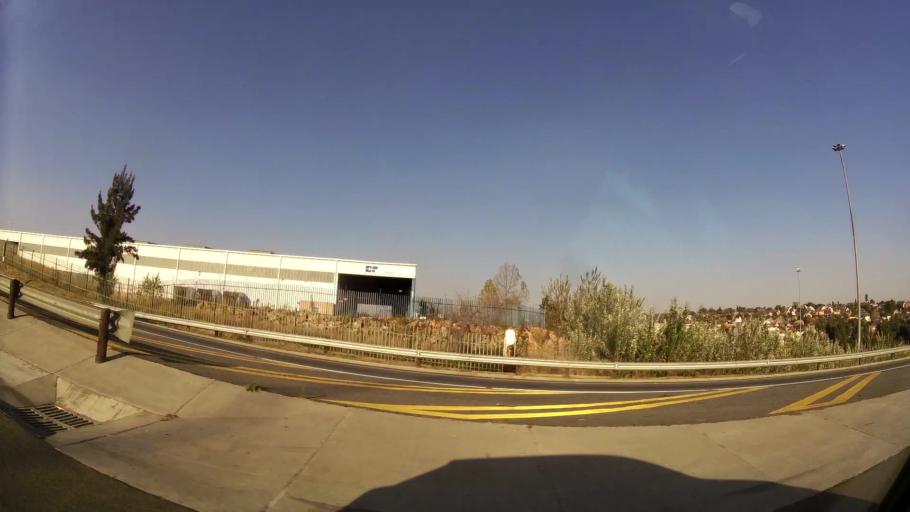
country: ZA
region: Gauteng
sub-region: Ekurhuleni Metropolitan Municipality
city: Germiston
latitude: -26.2440
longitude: 28.1250
